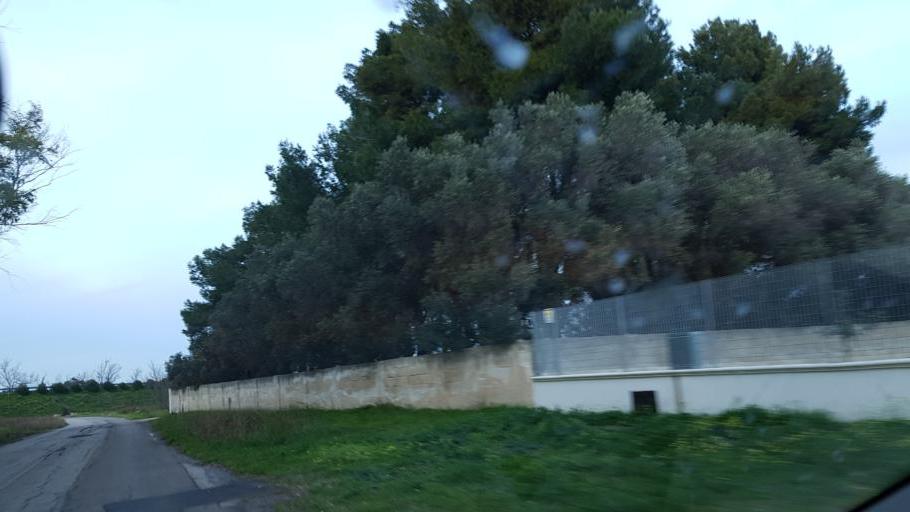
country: IT
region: Apulia
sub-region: Provincia di Brindisi
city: Brindisi
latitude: 40.6579
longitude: 17.9117
